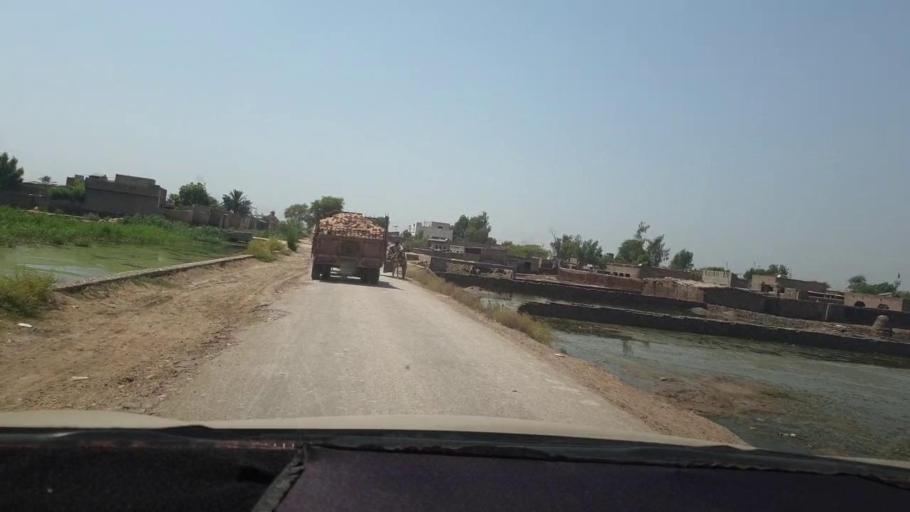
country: PK
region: Sindh
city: Shahdadkot
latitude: 27.8273
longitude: 67.9217
